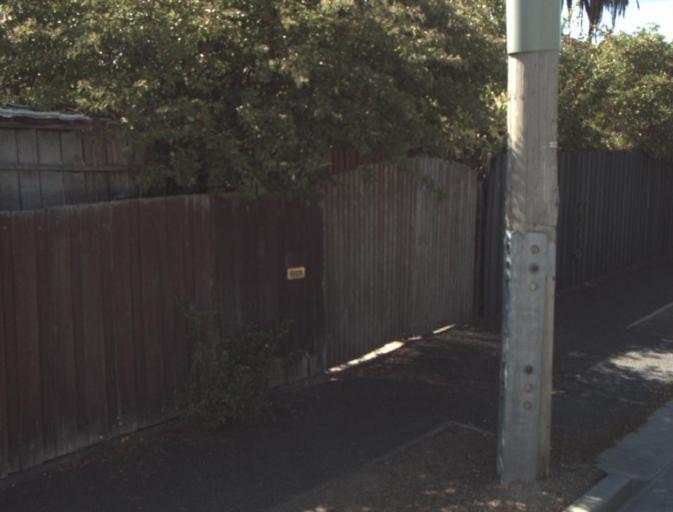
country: AU
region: Tasmania
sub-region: Launceston
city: Newnham
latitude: -41.4144
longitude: 147.1324
